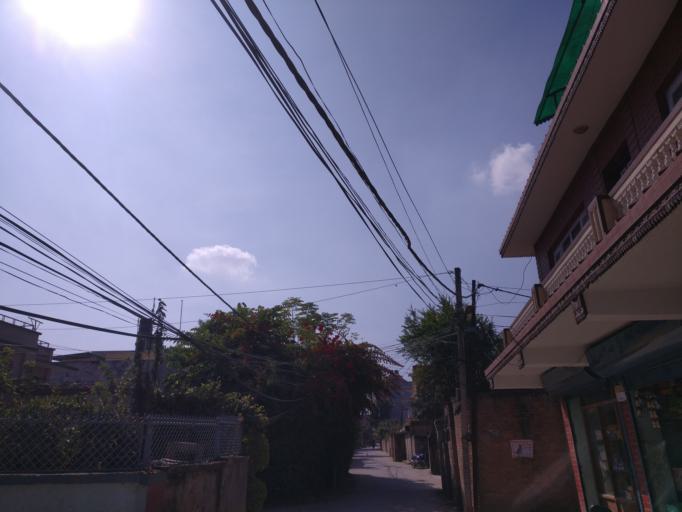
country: NP
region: Central Region
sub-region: Bagmati Zone
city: Patan
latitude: 27.6614
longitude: 85.3216
